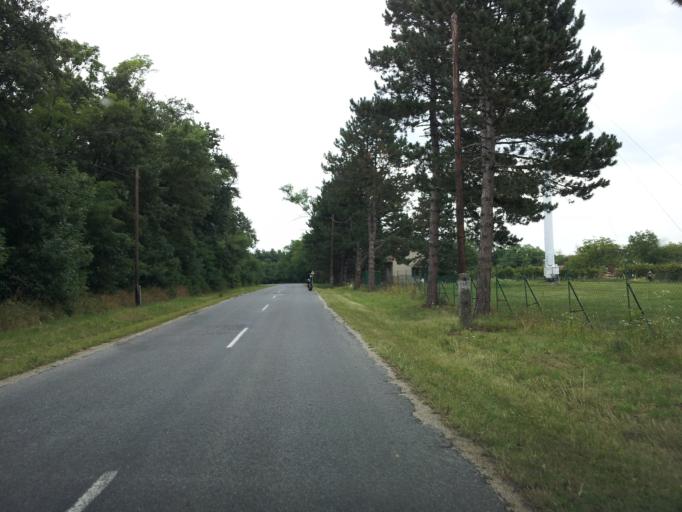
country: HU
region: Vas
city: Vasvar
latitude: 46.9822
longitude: 16.7437
